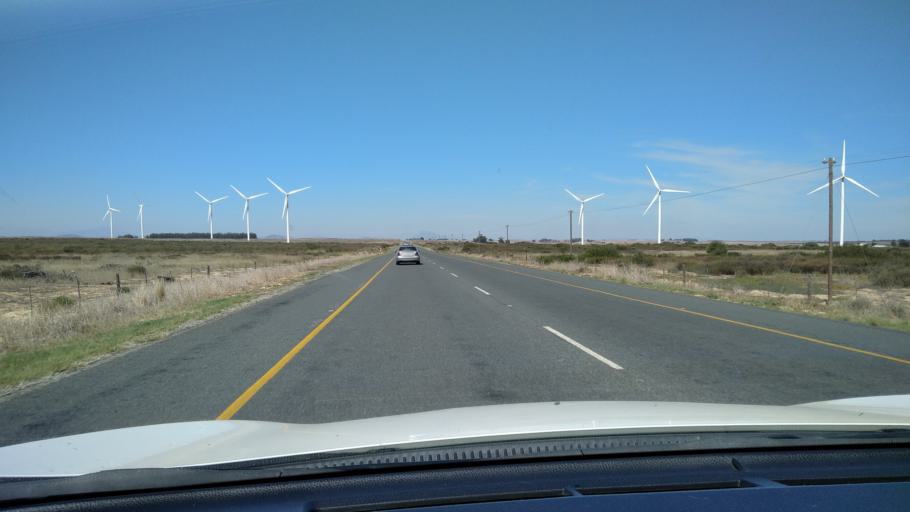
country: ZA
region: Western Cape
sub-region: West Coast District Municipality
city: Moorreesburg
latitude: -33.0849
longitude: 18.3966
